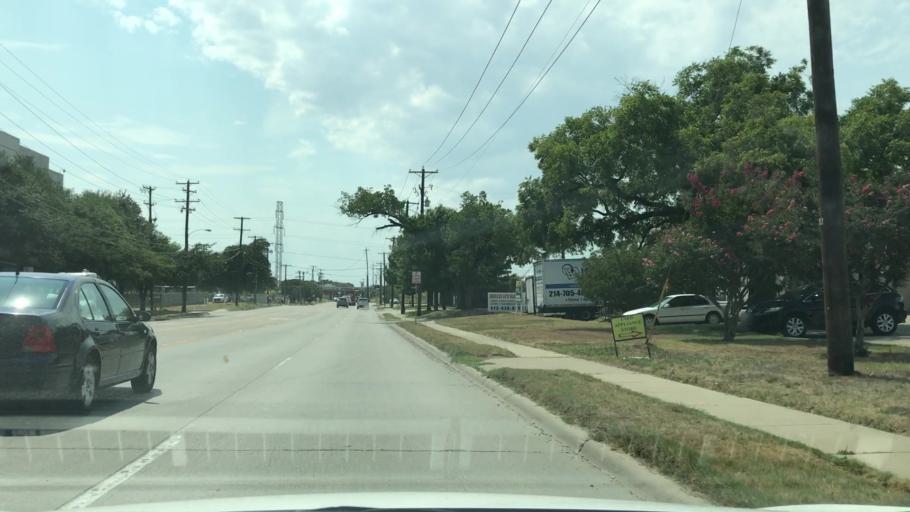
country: US
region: Texas
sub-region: Dallas County
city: Irving
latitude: 32.8308
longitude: -96.9123
